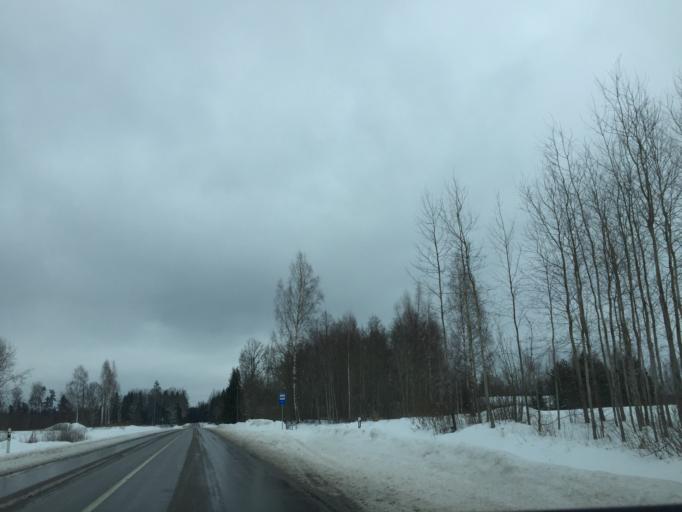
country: LV
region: Ligatne
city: Ligatne
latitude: 57.1725
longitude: 25.0431
